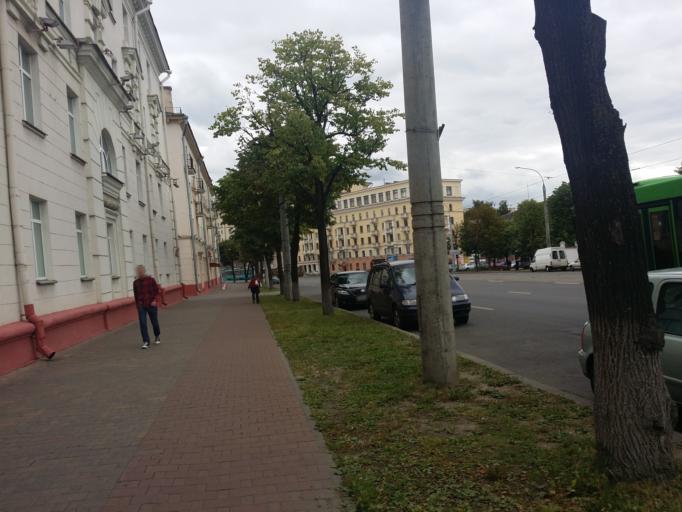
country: BY
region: Minsk
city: Minsk
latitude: 53.9123
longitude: 27.5762
